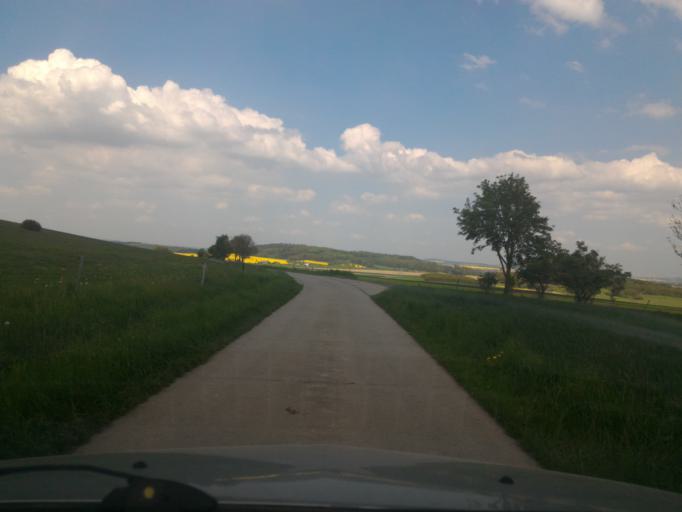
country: DE
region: Saxony
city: Bertsdorf-Hoernitz
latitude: 50.8888
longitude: 14.7108
